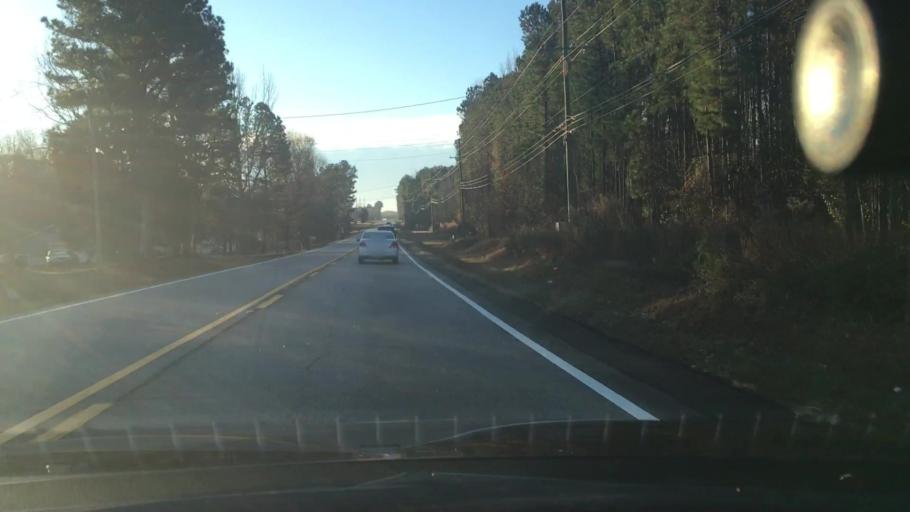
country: US
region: Georgia
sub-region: Fayette County
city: Peachtree City
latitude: 33.3918
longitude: -84.6766
